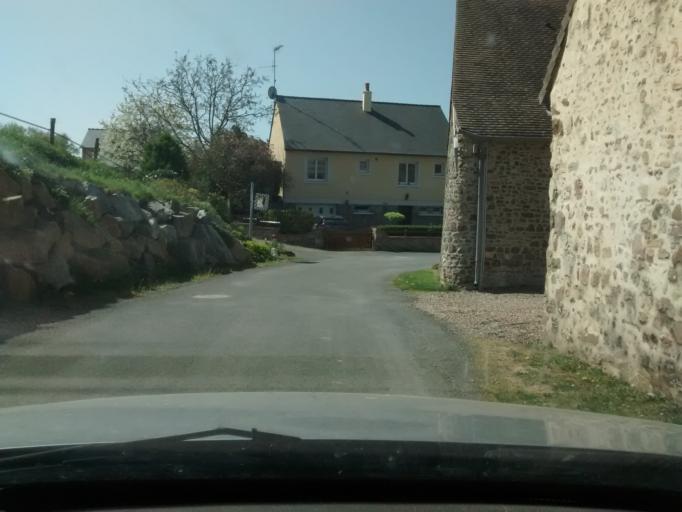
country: FR
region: Pays de la Loire
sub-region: Departement de la Mayenne
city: Sainte-Suzanne
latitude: 48.0911
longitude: -0.3535
